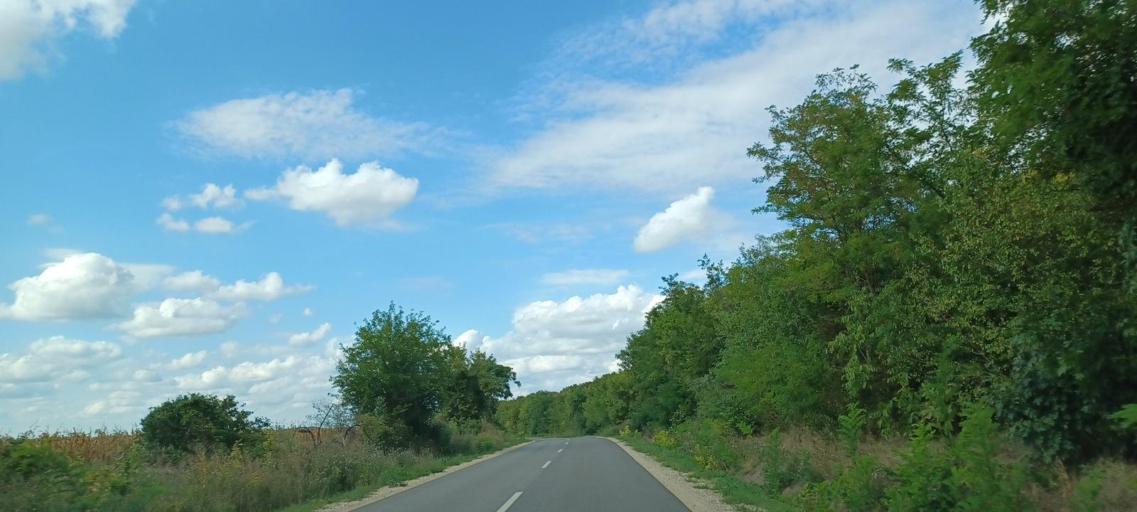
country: HU
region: Tolna
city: Zomba
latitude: 46.4403
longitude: 18.6077
